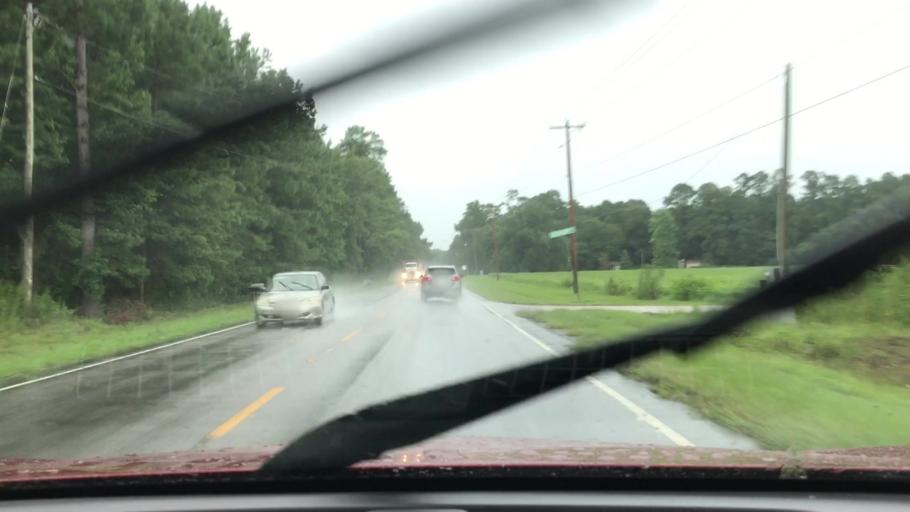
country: US
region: South Carolina
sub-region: Horry County
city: Conway
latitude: 33.7653
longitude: -79.0734
